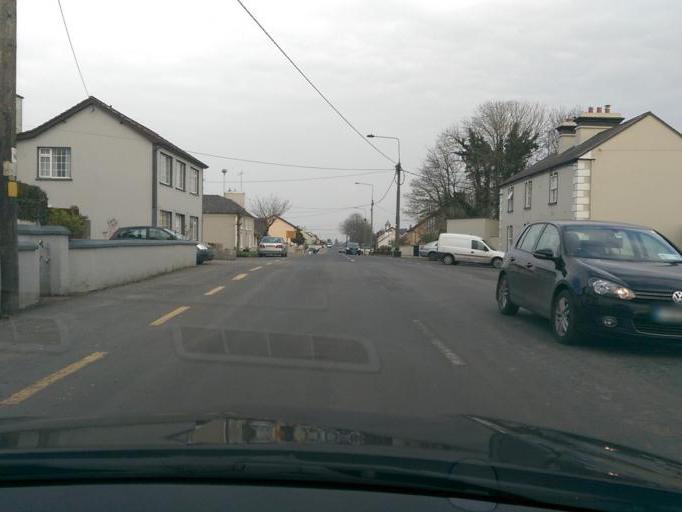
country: IE
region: Connaught
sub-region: Roscommon
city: Roscommon
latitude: 53.5210
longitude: -8.3309
